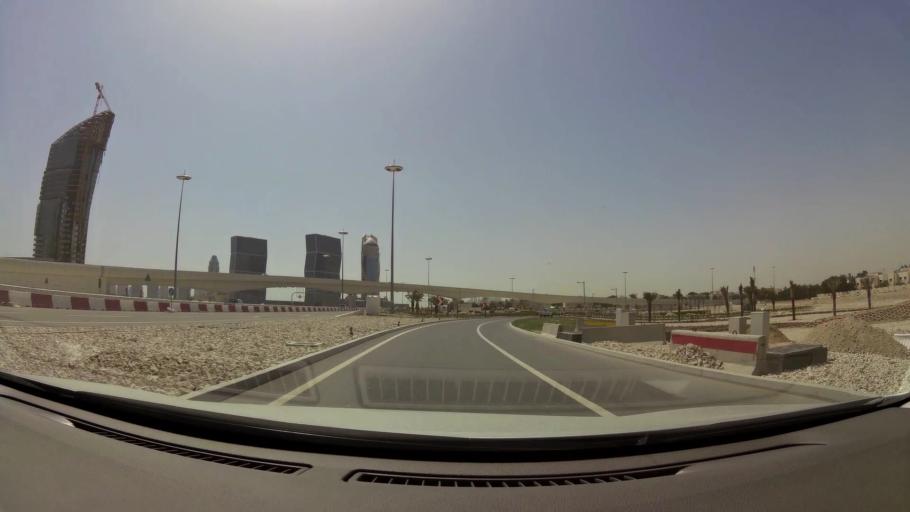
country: QA
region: Baladiyat ad Dawhah
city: Doha
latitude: 25.3842
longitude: 51.5199
